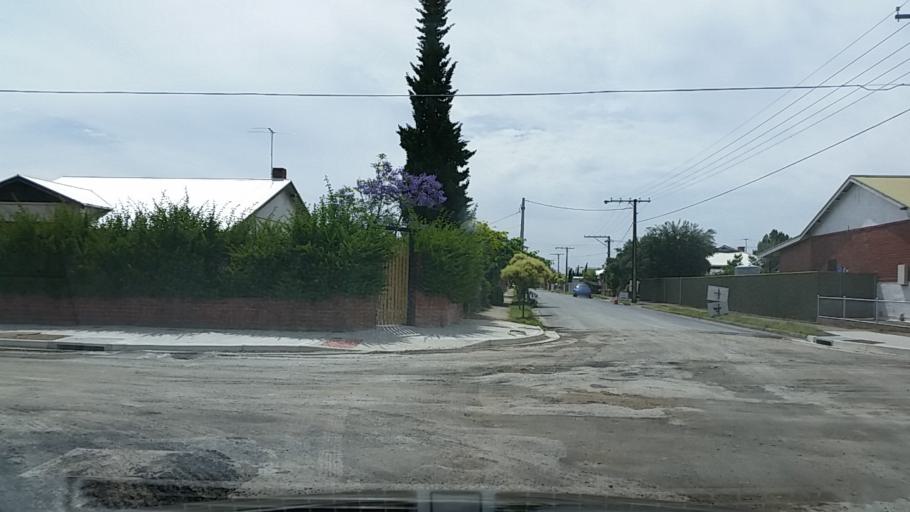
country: AU
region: South Australia
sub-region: Charles Sturt
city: Woodville
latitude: -34.8827
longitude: 138.5562
